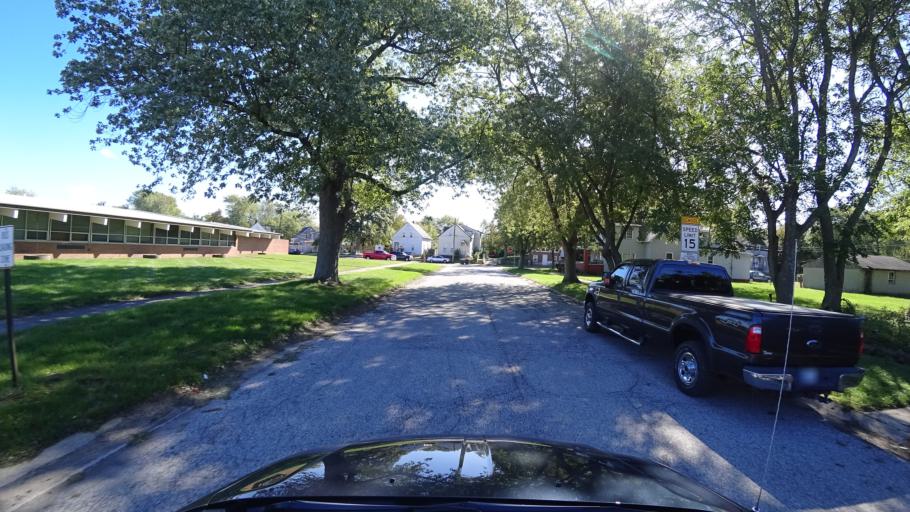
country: US
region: Indiana
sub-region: LaPorte County
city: Michigan City
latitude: 41.7114
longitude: -86.9157
